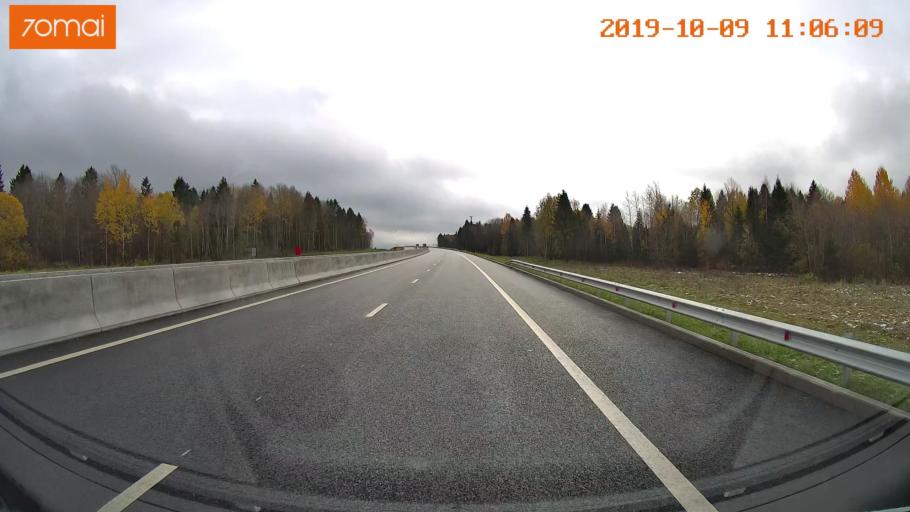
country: RU
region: Vologda
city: Molochnoye
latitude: 59.1902
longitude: 39.7587
